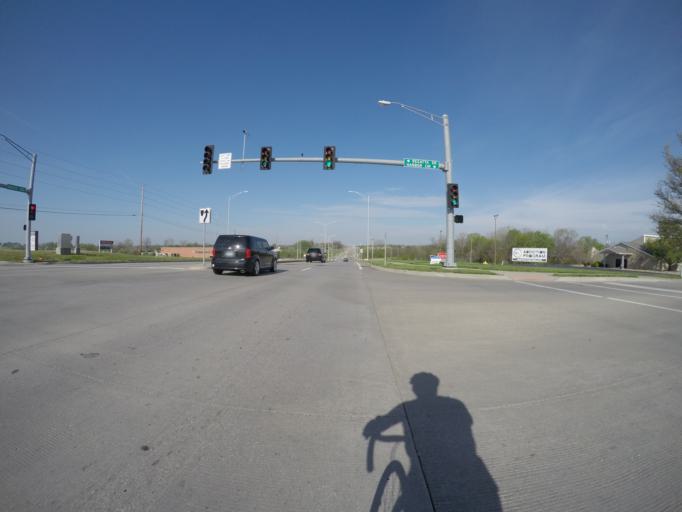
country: US
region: Missouri
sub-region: Cass County
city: Lake Winnebago
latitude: 38.8533
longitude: -94.3950
